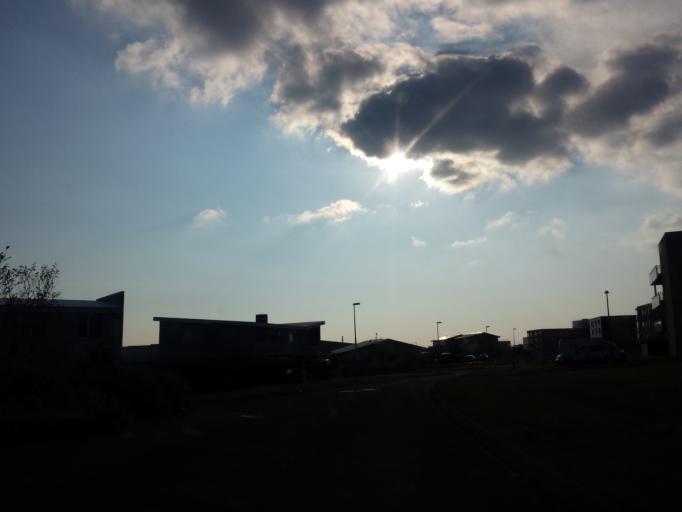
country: IS
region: Capital Region
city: Reykjavik
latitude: 64.0919
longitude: -21.8097
